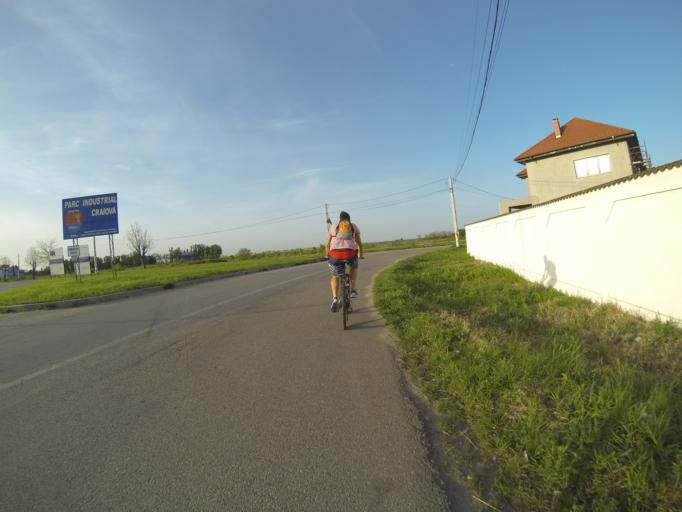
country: RO
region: Dolj
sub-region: Comuna Malu Mare
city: Preajba
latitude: 44.3225
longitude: 23.8670
